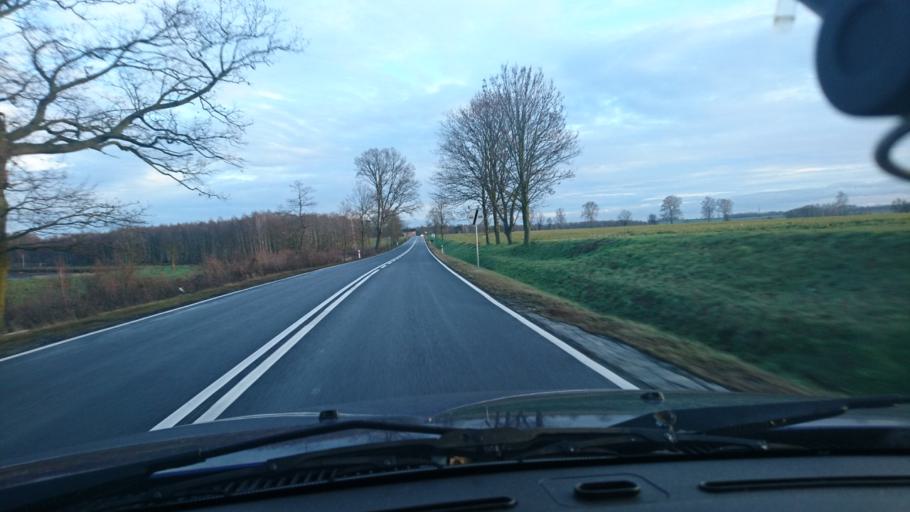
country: PL
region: Lodz Voivodeship
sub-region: Powiat wieruszowski
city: Boleslawiec
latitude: 51.1556
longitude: 18.1743
